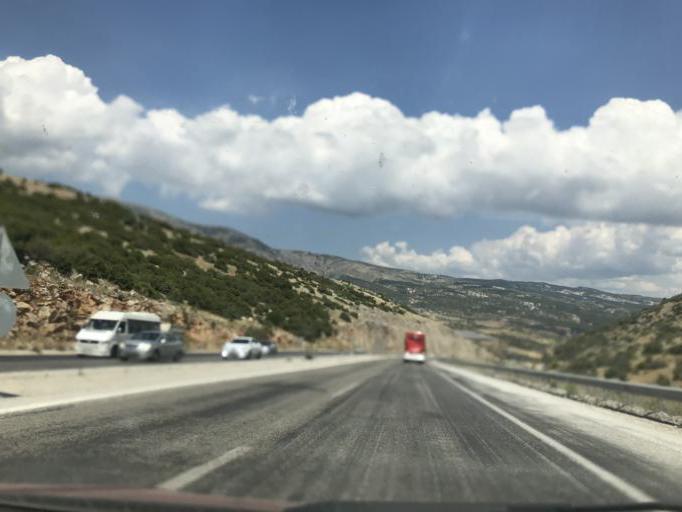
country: TR
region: Denizli
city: Serinhisar
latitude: 37.6195
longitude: 29.2518
